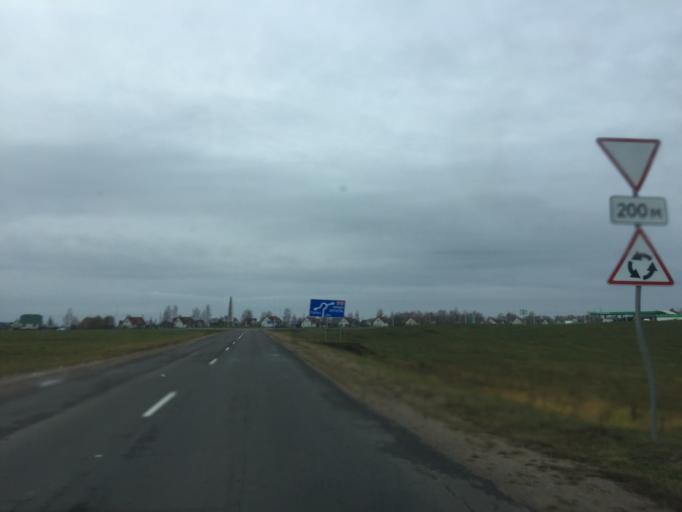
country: BY
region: Mogilev
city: Horki
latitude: 54.3093
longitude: 30.9432
